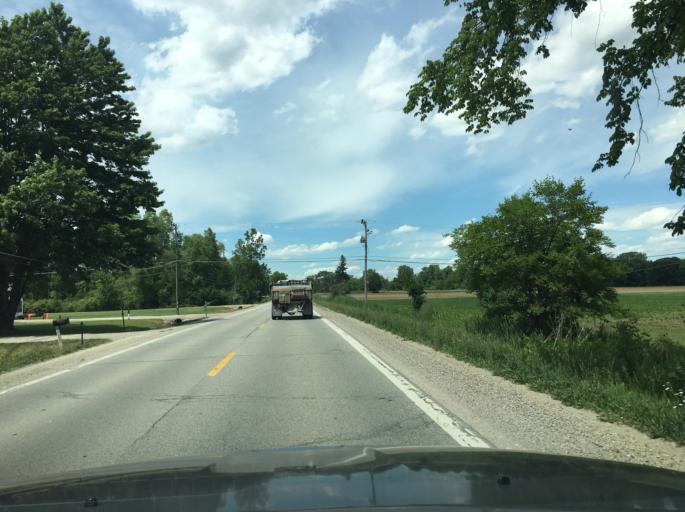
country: US
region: Michigan
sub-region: Macomb County
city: Romeo
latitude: 42.7675
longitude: -82.9613
